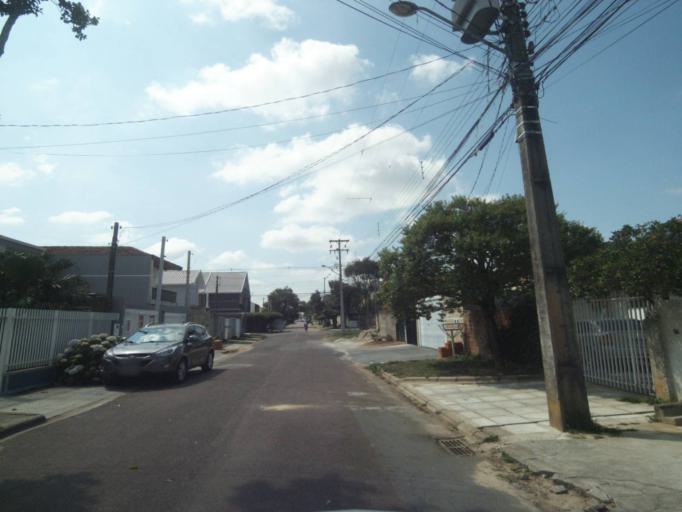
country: BR
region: Parana
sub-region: Sao Jose Dos Pinhais
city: Sao Jose dos Pinhais
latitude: -25.5402
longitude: -49.2663
